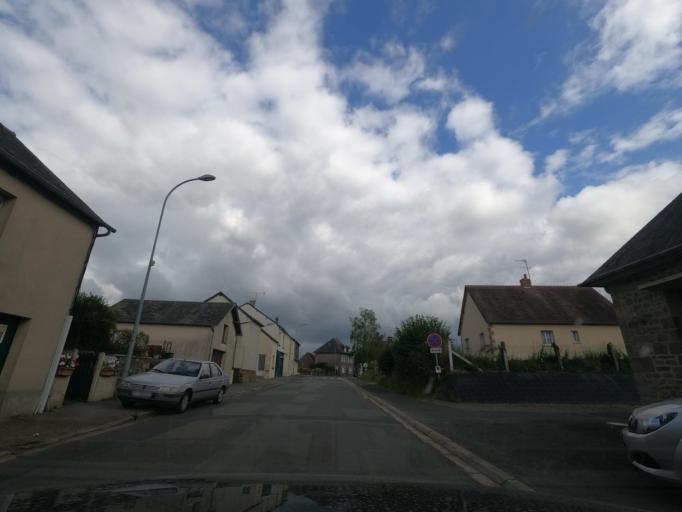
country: FR
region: Lower Normandy
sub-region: Departement de l'Orne
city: Briouze
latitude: 48.6906
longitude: -0.4445
